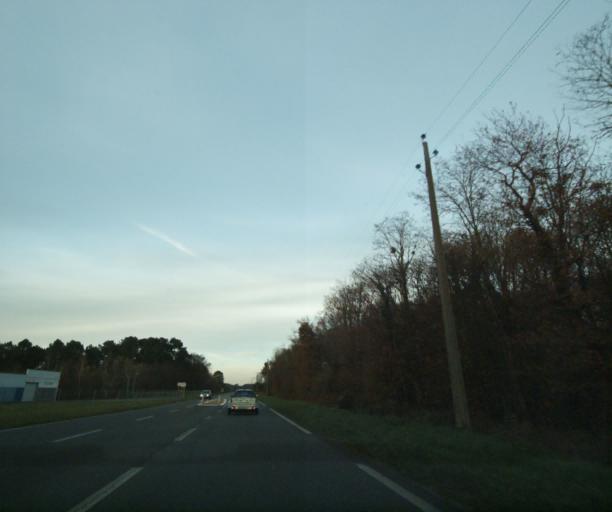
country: FR
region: Aquitaine
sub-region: Departement de la Gironde
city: Bazas
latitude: 44.4623
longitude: -0.2310
